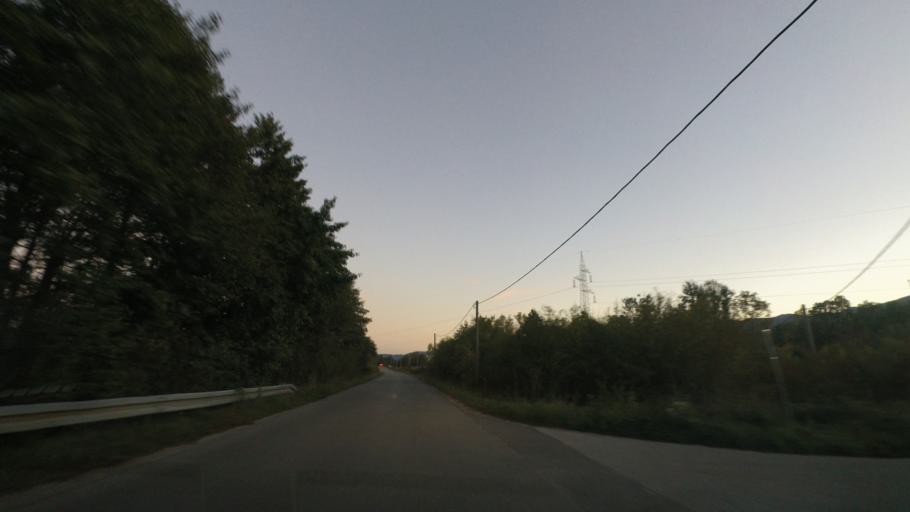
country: HR
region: Zadarska
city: Obrovac
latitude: 44.3711
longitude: 15.6466
